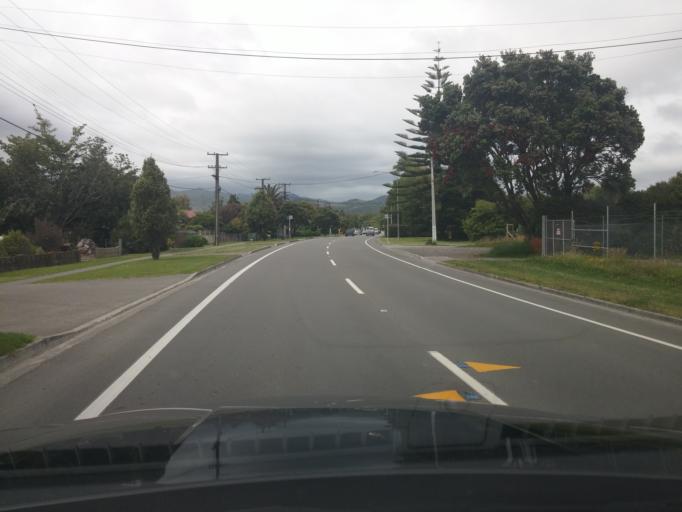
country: NZ
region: Wellington
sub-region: Kapiti Coast District
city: Paraparaumu
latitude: -40.8694
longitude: 175.0358
